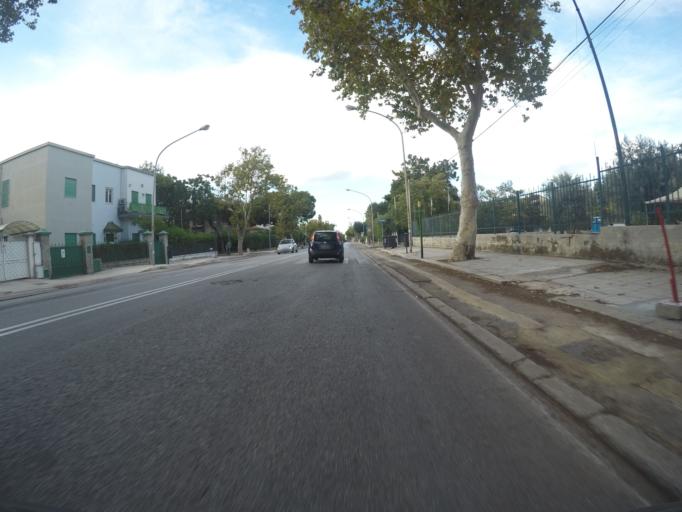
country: IT
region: Sicily
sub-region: Palermo
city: Palermo
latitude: 38.1911
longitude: 13.3327
